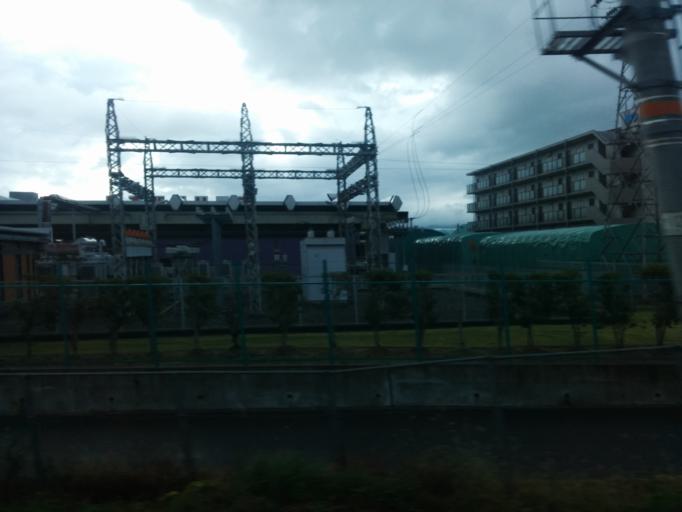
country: JP
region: Shiga Prefecture
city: Moriyama
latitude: 35.0436
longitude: 135.9875
